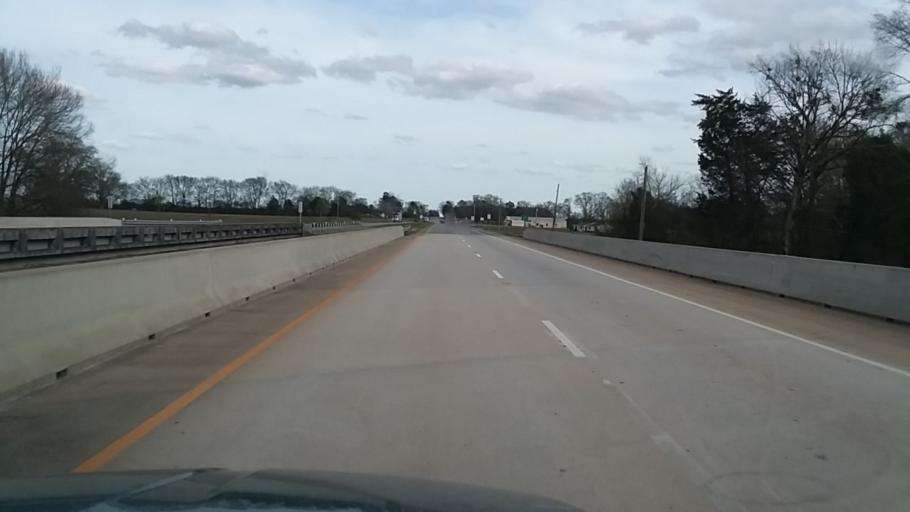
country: US
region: Alabama
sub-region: Lawrence County
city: Town Creek
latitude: 34.6822
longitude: -87.4514
